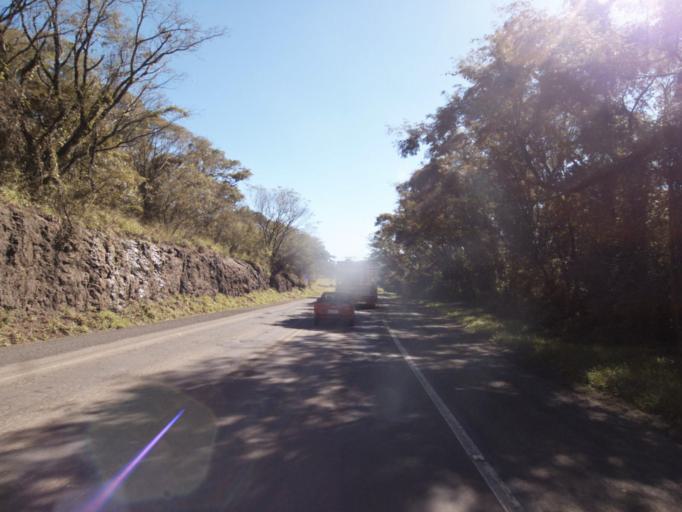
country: AR
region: Misiones
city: Bernardo de Irigoyen
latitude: -26.7690
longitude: -53.4795
